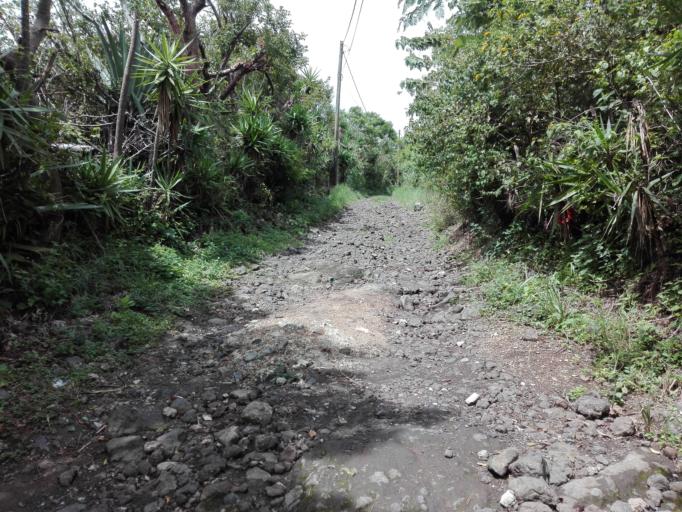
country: GT
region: Escuintla
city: San Vicente Pacaya
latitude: 14.3610
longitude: -90.5673
